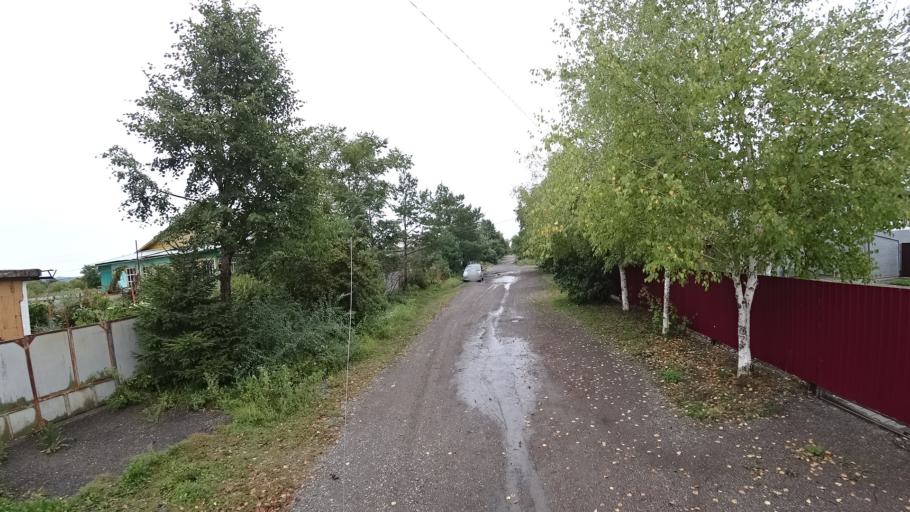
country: RU
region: Primorskiy
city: Monastyrishche
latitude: 44.2043
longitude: 132.4269
